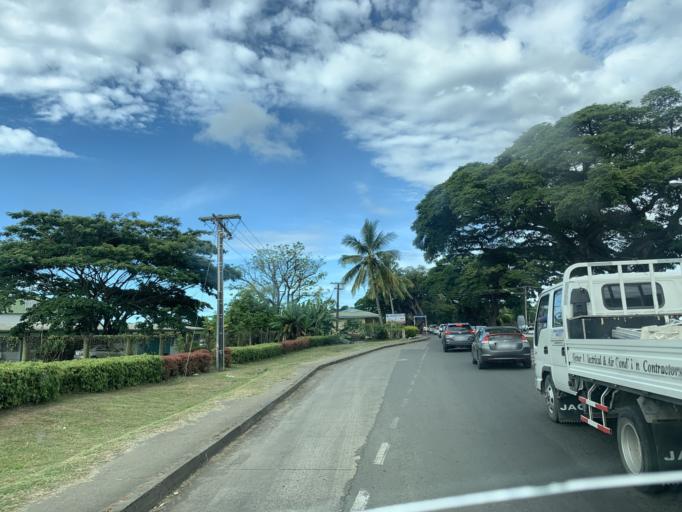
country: FJ
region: Western
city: Lautoka
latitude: -17.6176
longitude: 177.4439
